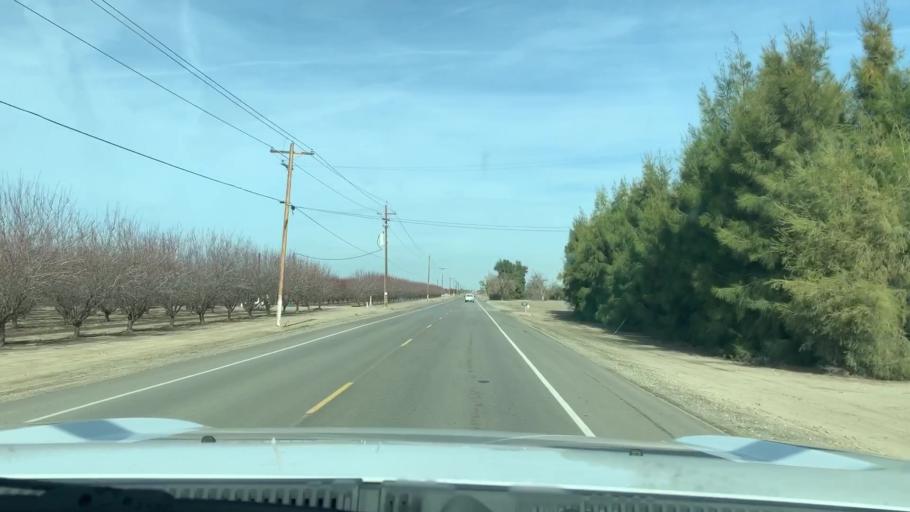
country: US
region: California
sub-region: Kern County
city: Buttonwillow
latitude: 35.5106
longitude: -119.4747
